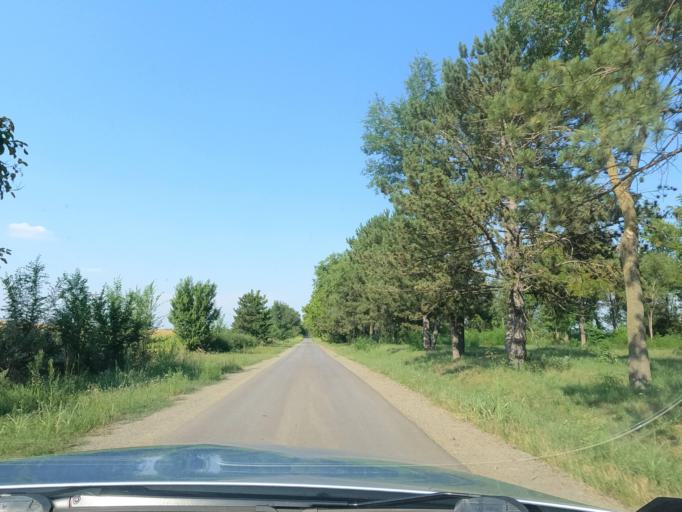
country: RS
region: Autonomna Pokrajina Vojvodina
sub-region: Juznobacki Okrug
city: Becej
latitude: 45.6612
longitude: 19.9057
